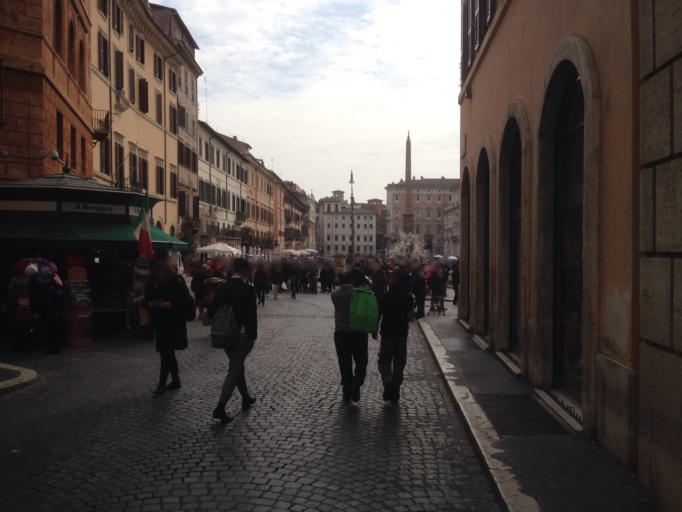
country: VA
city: Vatican City
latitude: 41.9003
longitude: 12.4731
